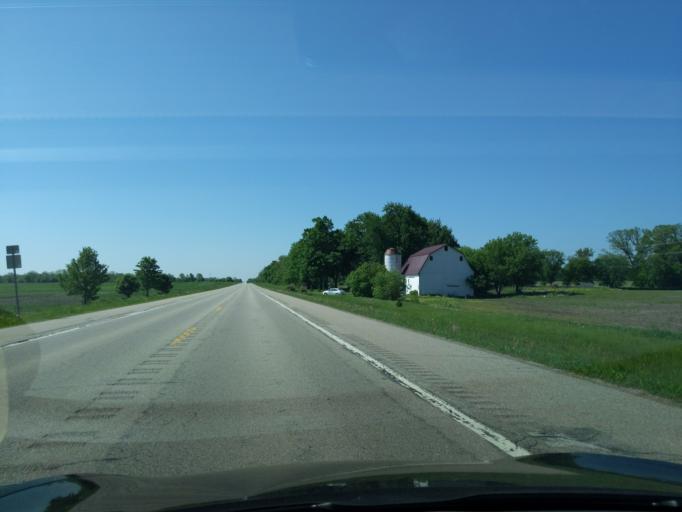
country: US
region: Michigan
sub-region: Ingham County
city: Stockbridge
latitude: 42.5477
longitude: -84.1915
